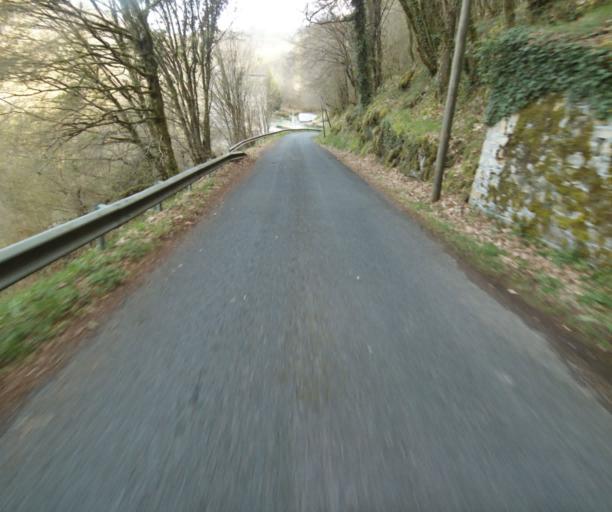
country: FR
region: Limousin
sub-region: Departement de la Correze
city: Correze
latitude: 45.3432
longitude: 1.8237
